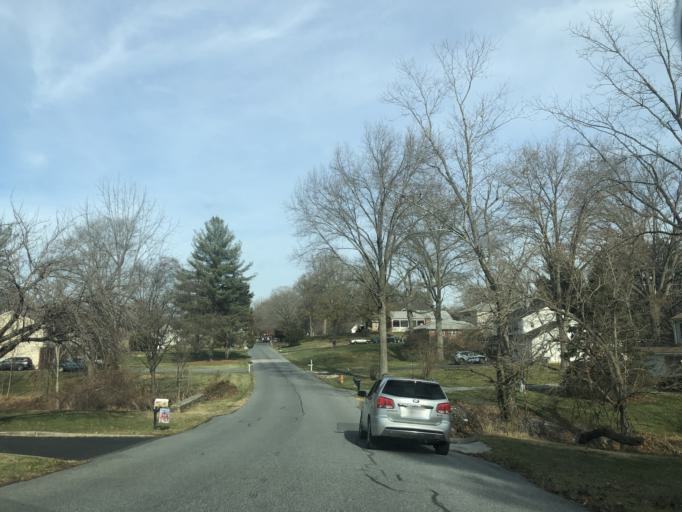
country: US
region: Maryland
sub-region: Howard County
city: Columbia
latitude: 39.2815
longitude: -76.8431
